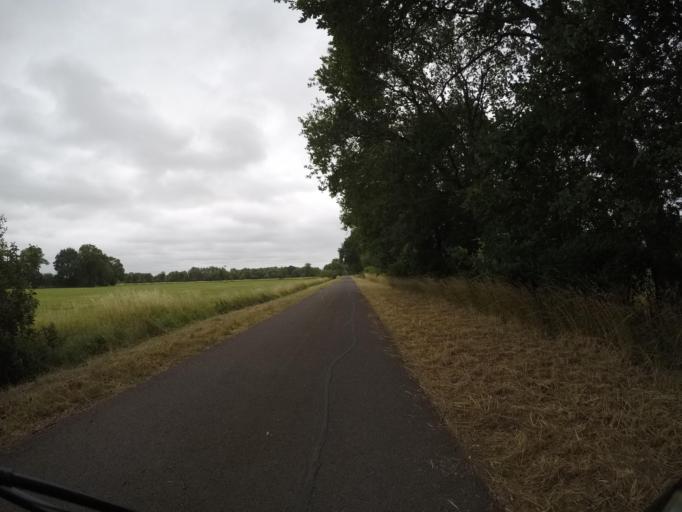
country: DE
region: Lower Saxony
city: Hitzacker
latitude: 53.1553
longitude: 11.0852
